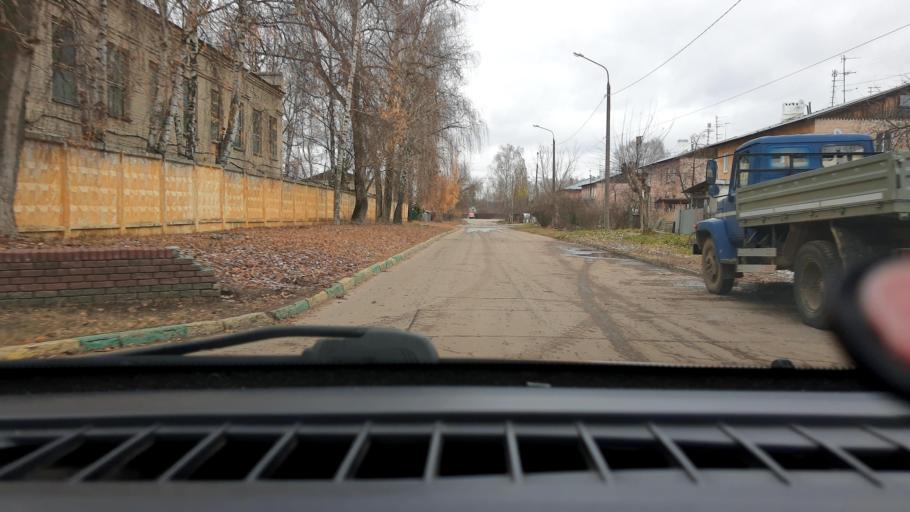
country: RU
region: Nizjnij Novgorod
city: Gorbatovka
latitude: 56.3821
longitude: 43.7835
